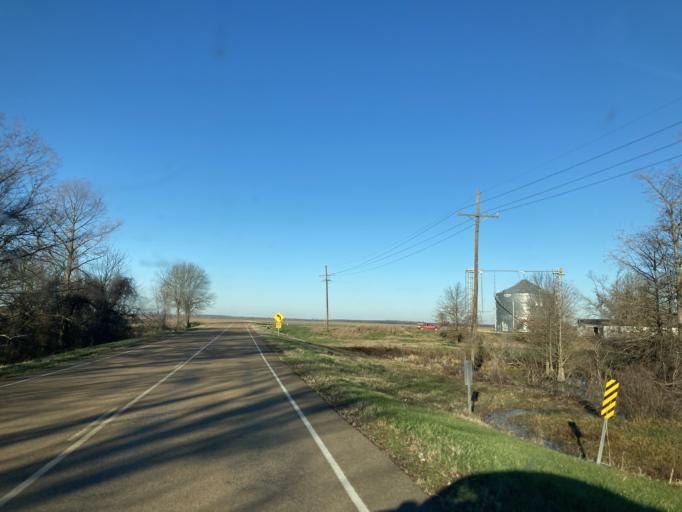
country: US
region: Mississippi
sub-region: Yazoo County
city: Yazoo City
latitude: 32.9305
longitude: -90.5984
